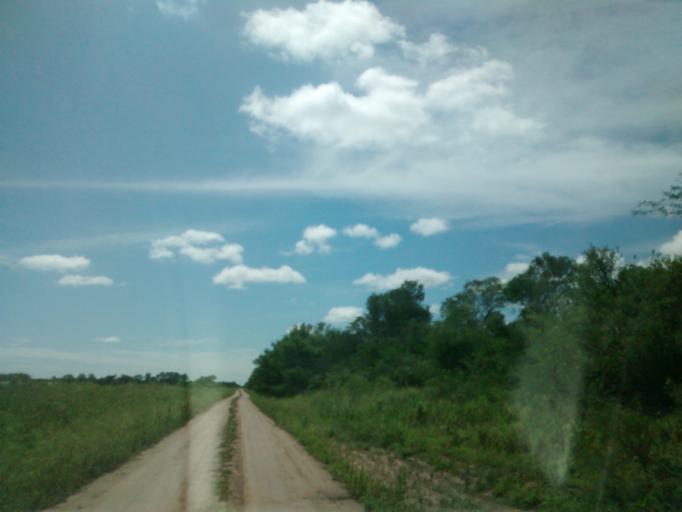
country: AR
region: Chaco
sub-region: Departamento de Quitilipi
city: Quitilipi
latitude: -26.7768
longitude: -60.2420
